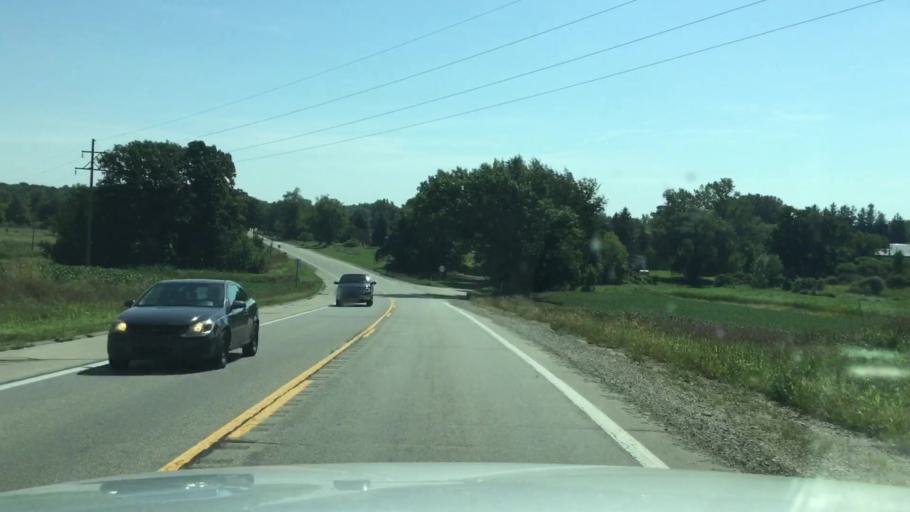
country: US
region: Michigan
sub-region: Lenawee County
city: Manitou Beach-Devils Lake
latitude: 42.0102
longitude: -84.3027
